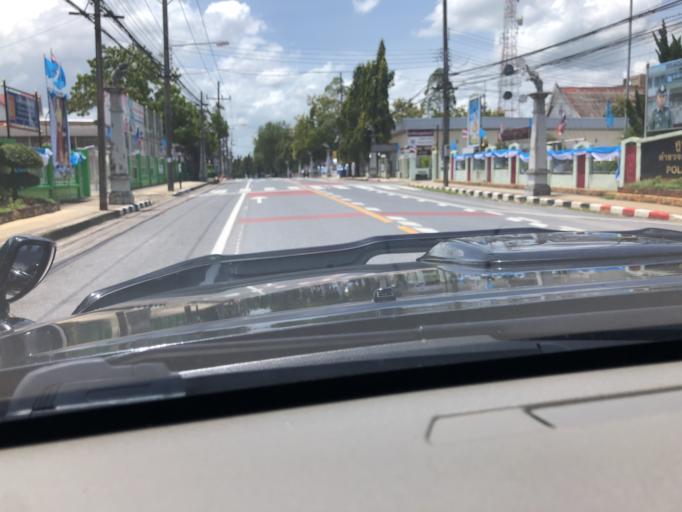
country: TH
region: Krabi
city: Krabi
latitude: 8.0562
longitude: 98.9176
